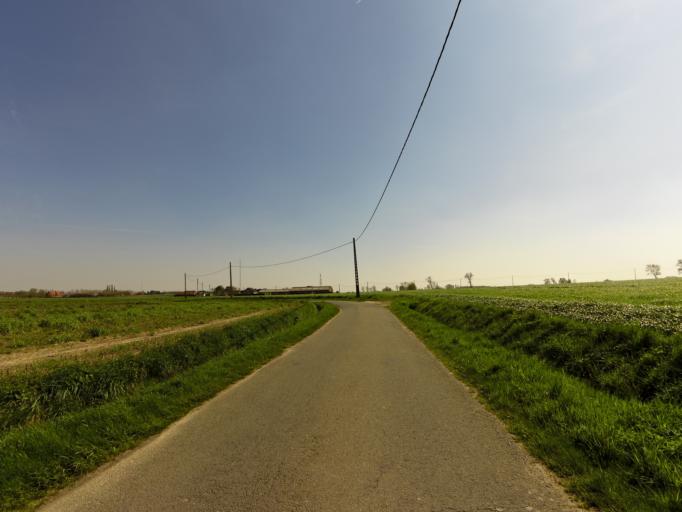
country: BE
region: Flanders
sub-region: Provincie West-Vlaanderen
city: Ichtegem
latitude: 51.0771
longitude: 3.0075
